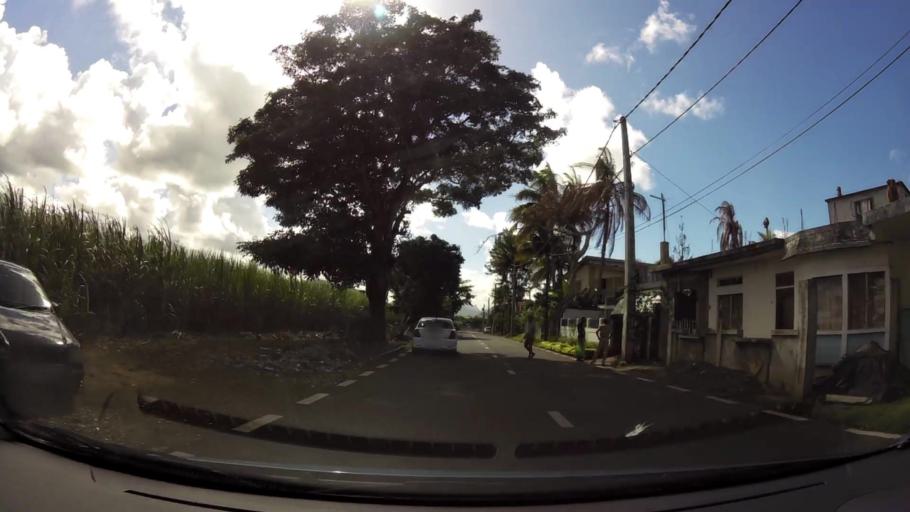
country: MU
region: Grand Port
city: Plaine Magnien
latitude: -20.4270
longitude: 57.6683
